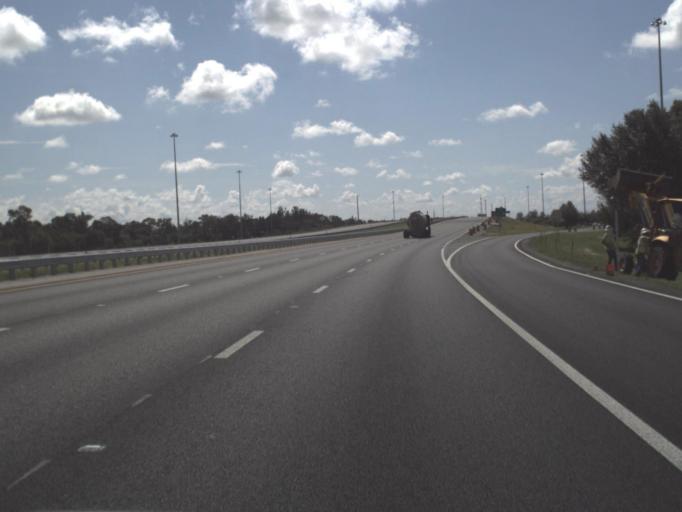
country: US
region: Florida
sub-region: Lee County
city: Tice
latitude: 26.7187
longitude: -81.8149
